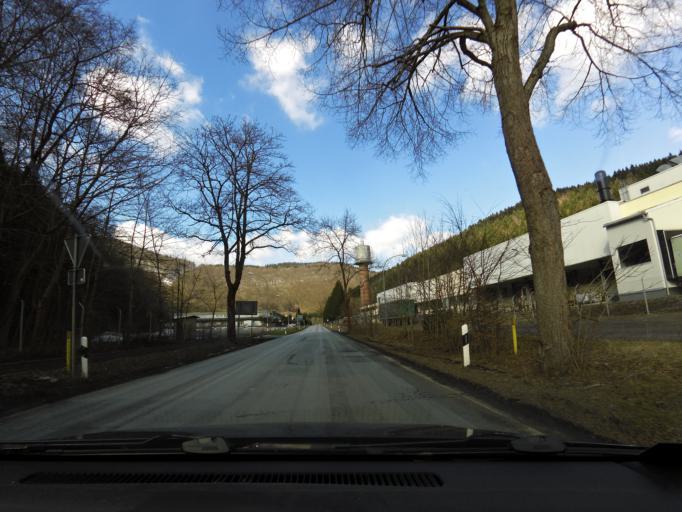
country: DE
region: Lower Saxony
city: Bad Lauterberg im Harz
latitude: 51.6457
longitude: 10.4894
